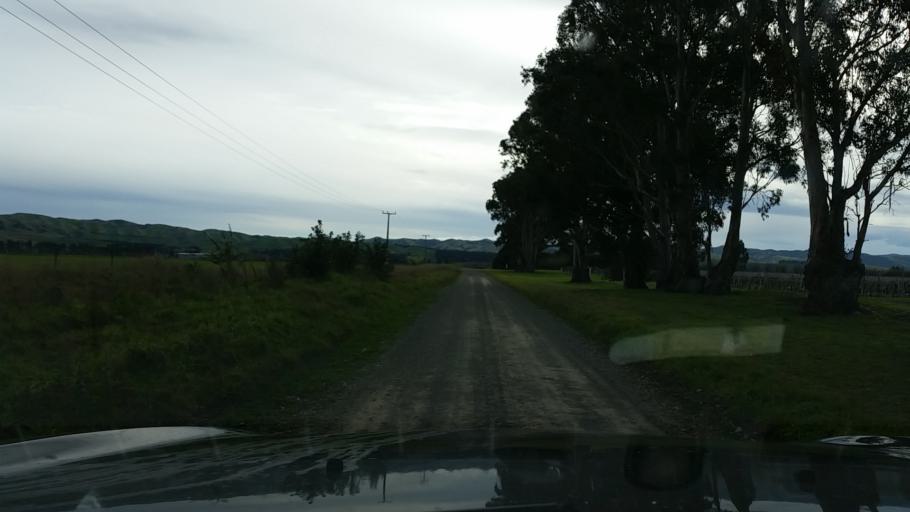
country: NZ
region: Marlborough
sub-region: Marlborough District
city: Blenheim
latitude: -41.6368
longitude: 174.1207
